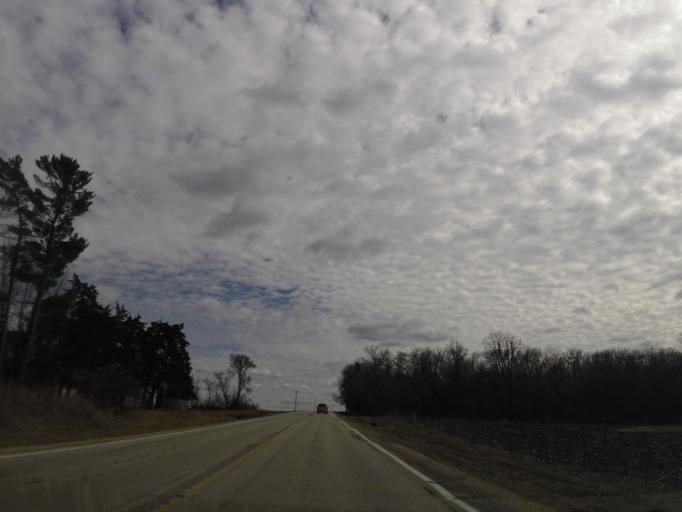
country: US
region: Minnesota
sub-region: Olmsted County
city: Stewartville
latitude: 43.8782
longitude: -92.4041
